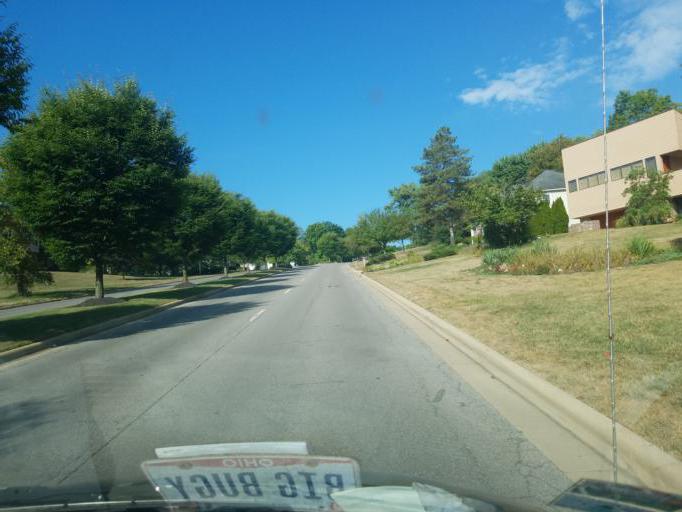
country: US
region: Ohio
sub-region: Franklin County
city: Worthington
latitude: 40.1249
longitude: -83.0382
